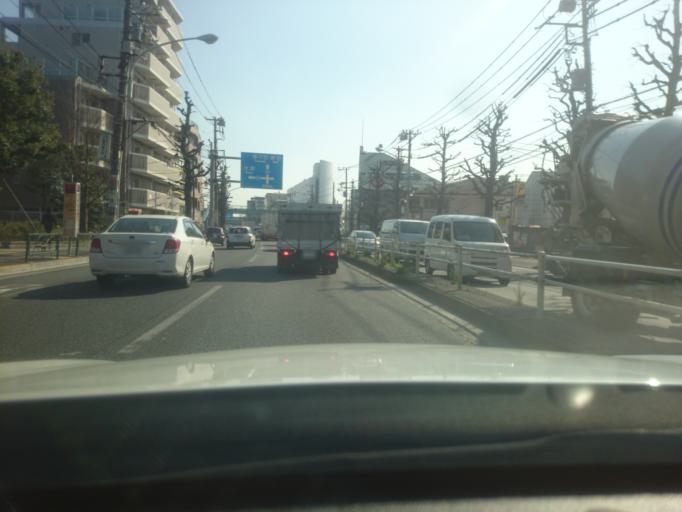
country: JP
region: Tokyo
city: Mitaka-shi
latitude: 35.6809
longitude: 139.6148
